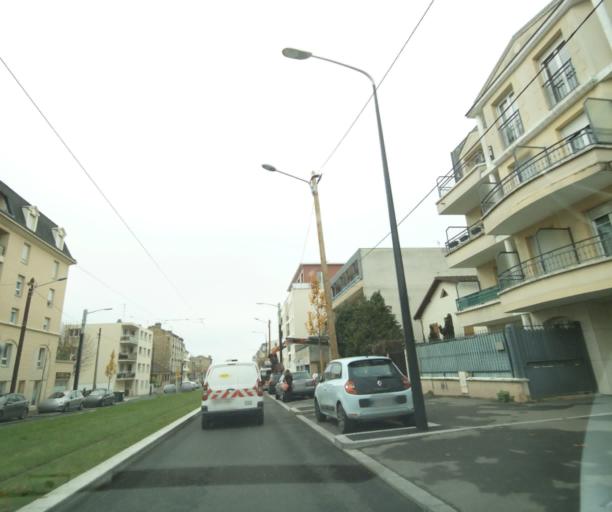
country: FR
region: Ile-de-France
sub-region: Departement de Seine-Saint-Denis
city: Le Raincy
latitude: 48.9068
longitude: 2.5215
